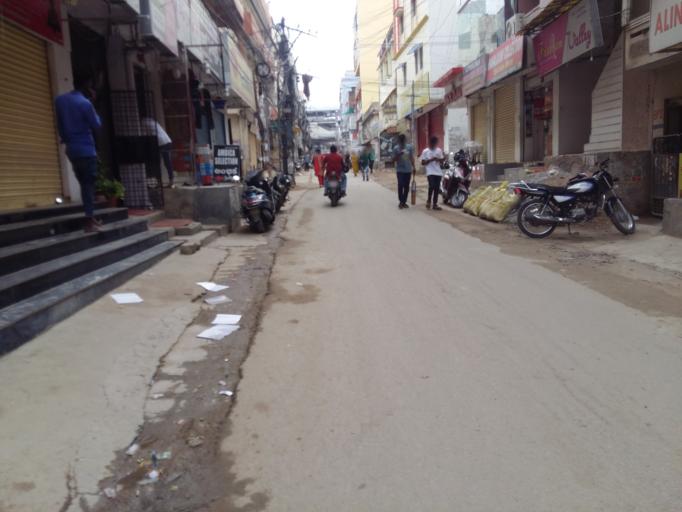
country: IN
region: Telangana
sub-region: Rangareddi
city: Kukatpalli
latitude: 17.4923
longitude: 78.4004
